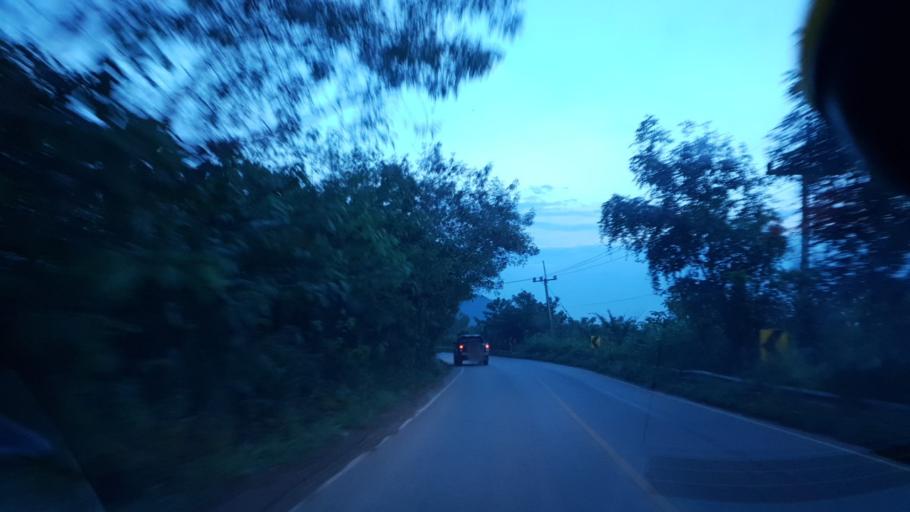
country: TH
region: Chiang Rai
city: Wiang Chiang Rung
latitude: 19.9657
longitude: 99.9840
